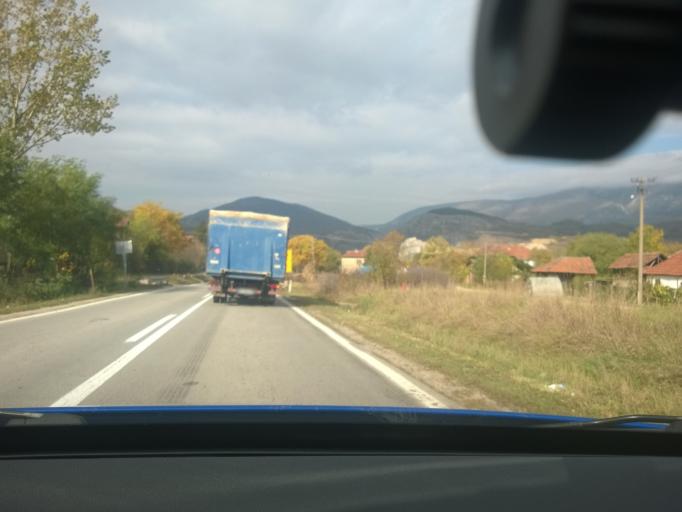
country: RS
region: Central Serbia
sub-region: Pirotski Okrug
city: Bela Palanka
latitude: 43.2970
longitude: 22.2025
